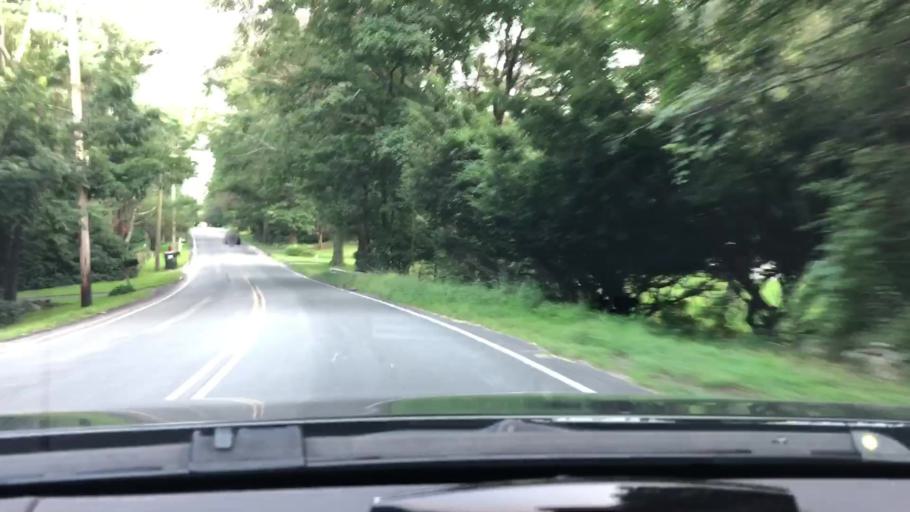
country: US
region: Massachusetts
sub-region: Norfolk County
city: Millis-Clicquot
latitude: 42.1713
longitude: -71.3449
